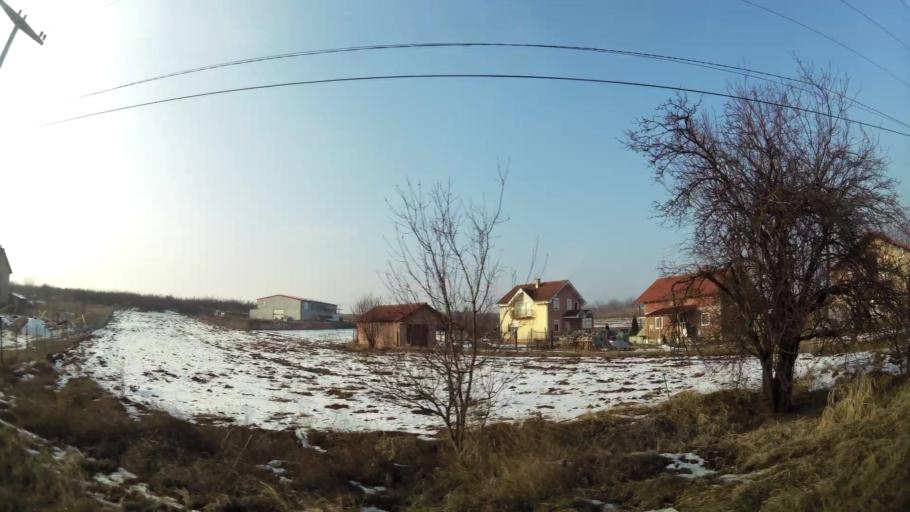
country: MK
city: Miladinovci
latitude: 41.9795
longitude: 21.6462
